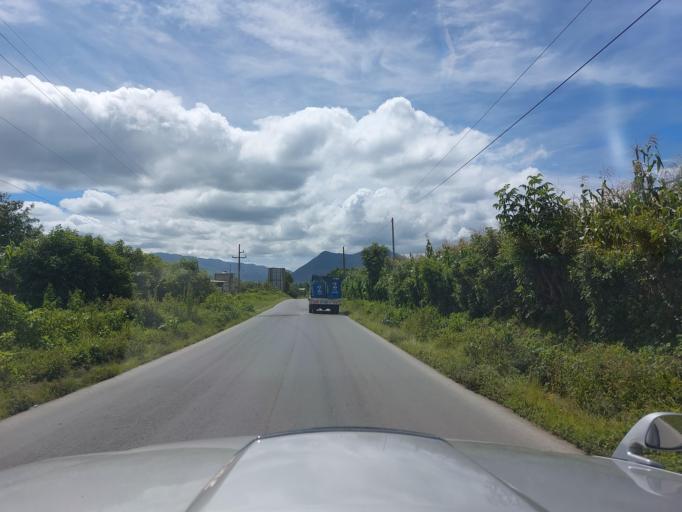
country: GT
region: Chimaltenango
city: San Andres Itzapa
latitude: 14.6181
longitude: -90.8307
